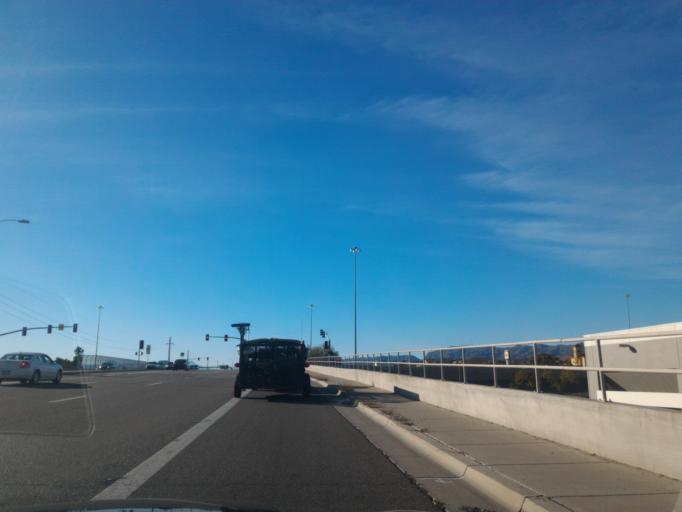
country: US
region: Arizona
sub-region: Maricopa County
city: Guadalupe
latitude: 33.3055
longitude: -111.9701
